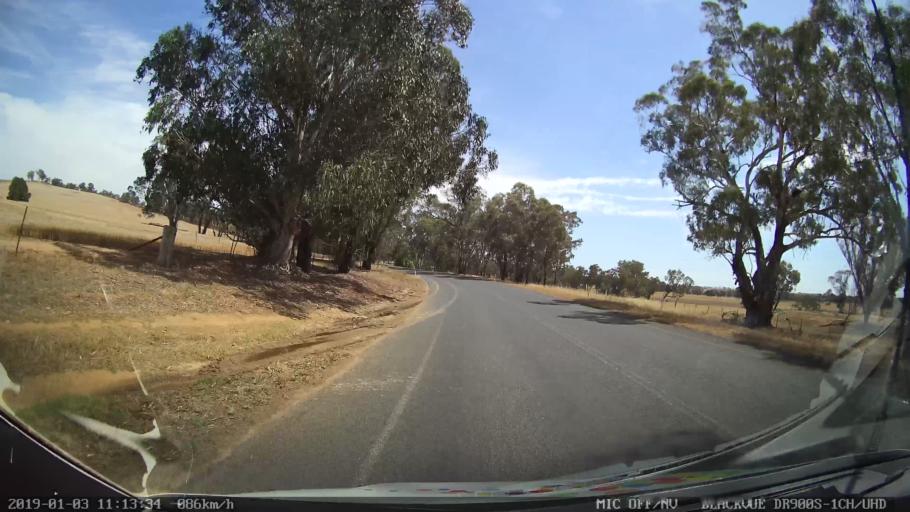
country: AU
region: New South Wales
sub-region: Young
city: Young
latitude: -34.1869
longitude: 148.2607
